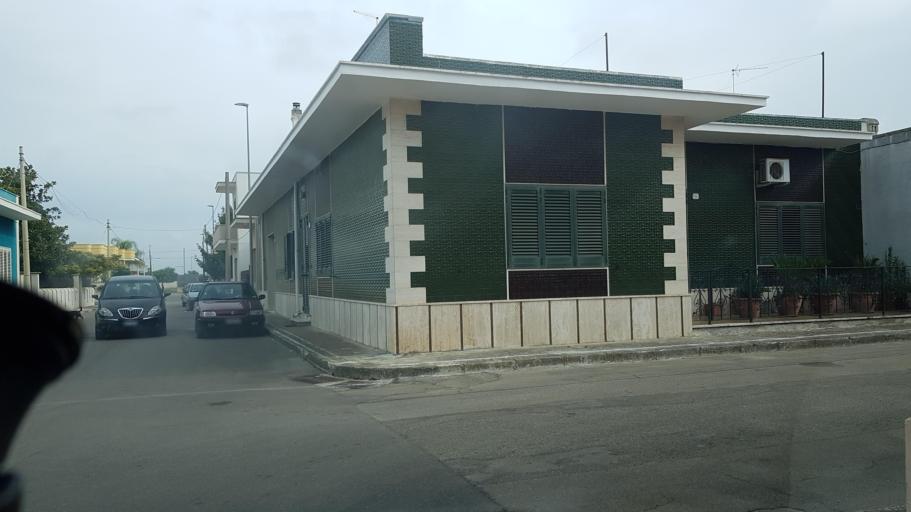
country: IT
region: Apulia
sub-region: Provincia di Lecce
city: Guagnano
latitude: 40.4045
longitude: 17.9490
